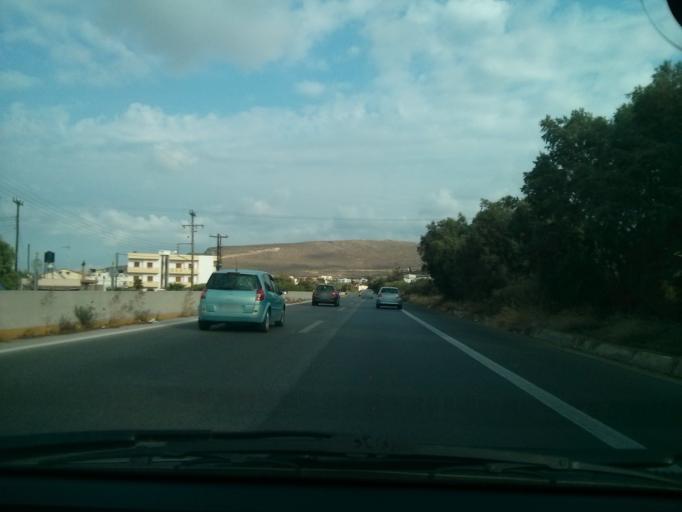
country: GR
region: Crete
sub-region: Nomos Irakleiou
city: Kokkini Hani
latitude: 35.3280
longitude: 25.2498
